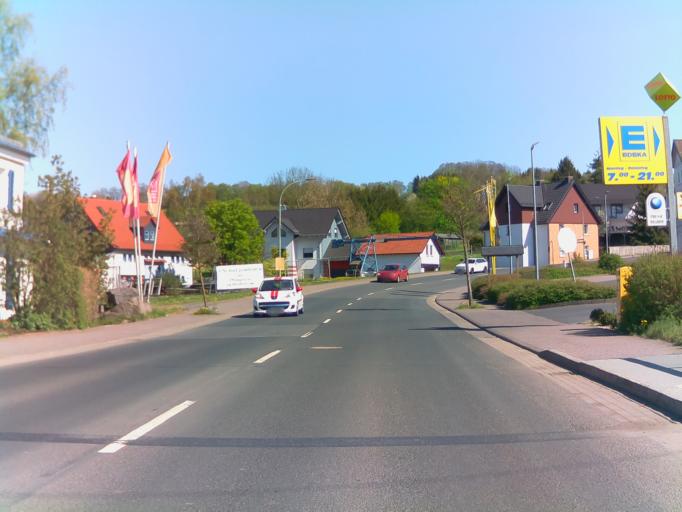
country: DE
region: Hesse
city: Herbstein
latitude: 50.5565
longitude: 9.3508
